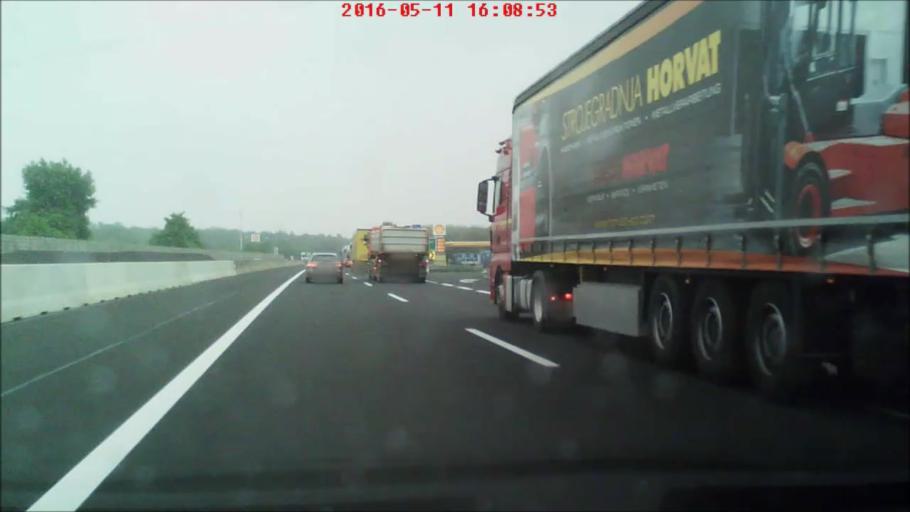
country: AT
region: Styria
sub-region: Politischer Bezirk Leibnitz
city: Lang
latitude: 46.8360
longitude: 15.5445
